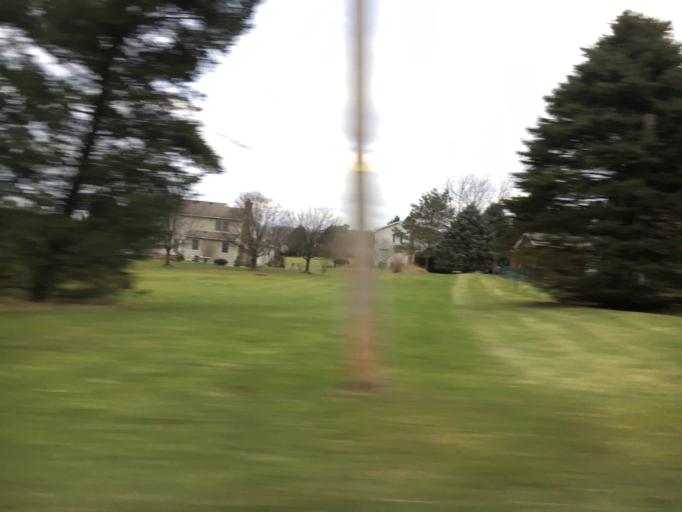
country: US
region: Pennsylvania
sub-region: Lehigh County
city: Schnecksville
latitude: 40.6844
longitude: -75.5841
